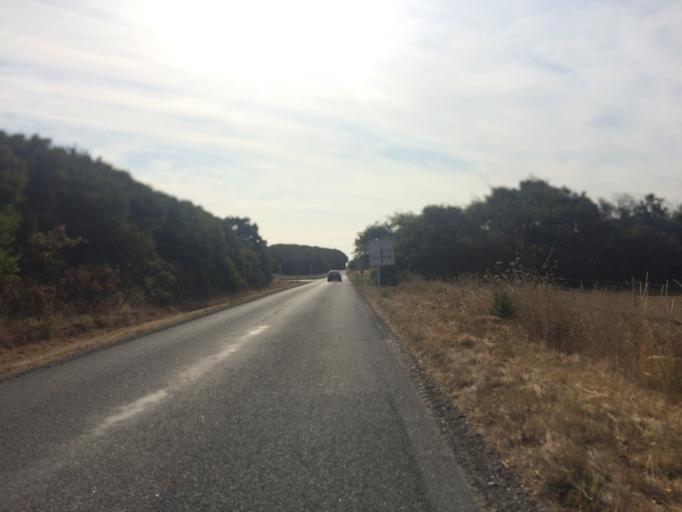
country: DK
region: North Denmark
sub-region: Morso Kommune
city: Nykobing Mors
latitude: 56.6515
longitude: 8.7828
